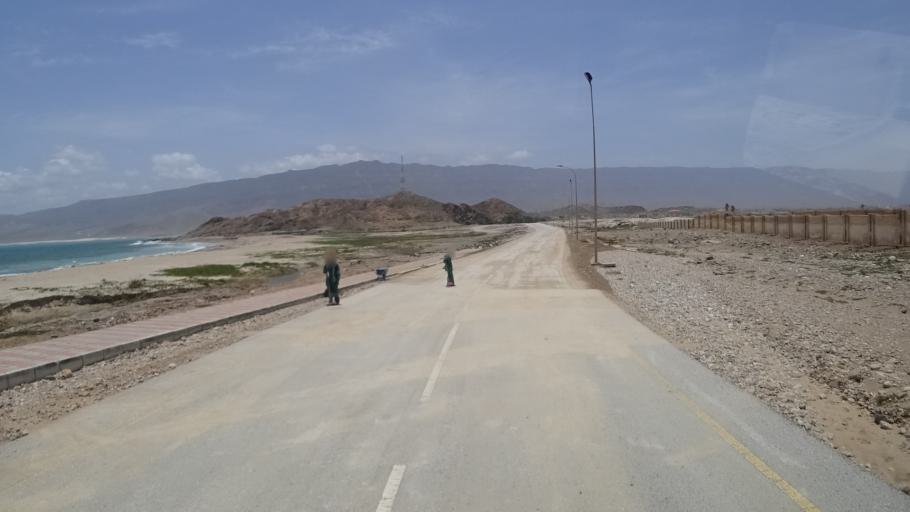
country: OM
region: Zufar
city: Salalah
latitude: 16.9933
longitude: 54.6915
